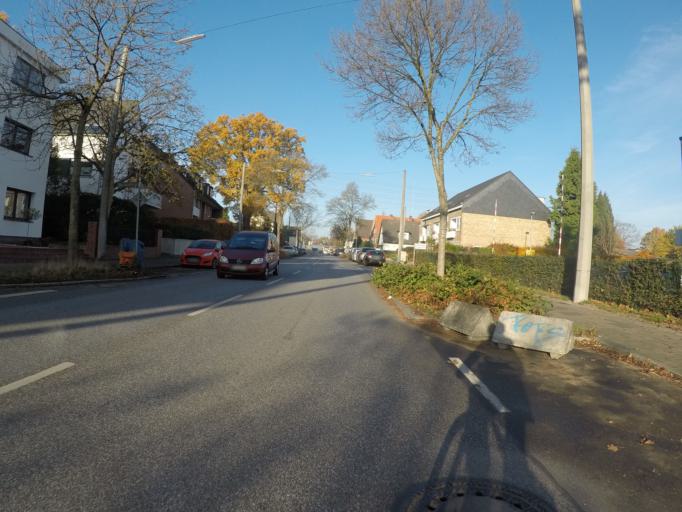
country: DE
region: Hamburg
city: Eidelstedt
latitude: 53.6307
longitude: 9.9259
